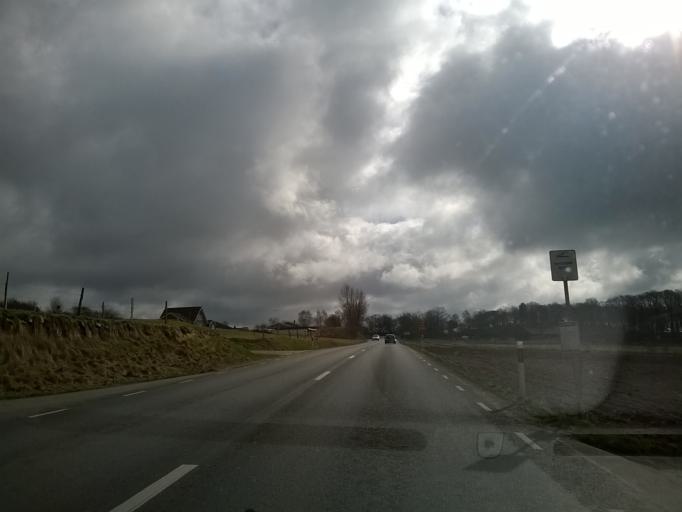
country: SE
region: Halland
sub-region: Varbergs Kommun
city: Tvaaker
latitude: 57.1461
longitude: 12.4470
